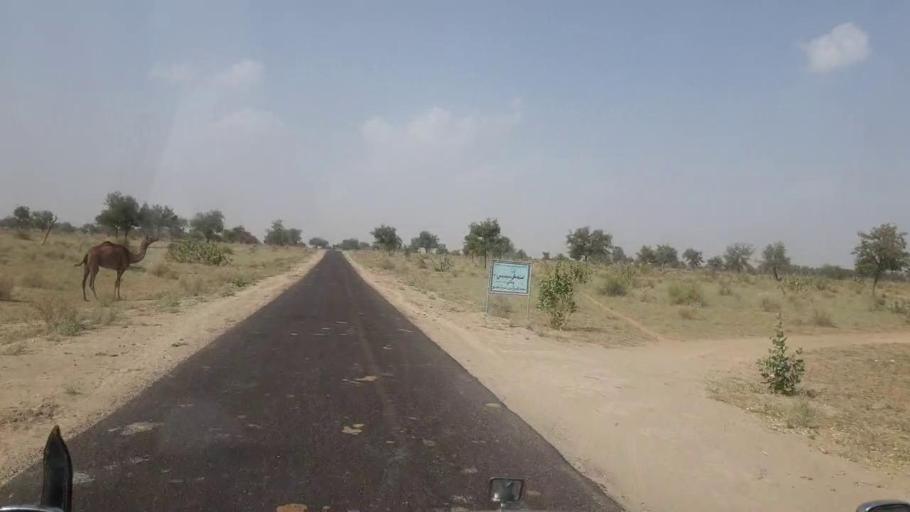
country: PK
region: Sindh
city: Islamkot
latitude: 25.1710
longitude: 70.2886
